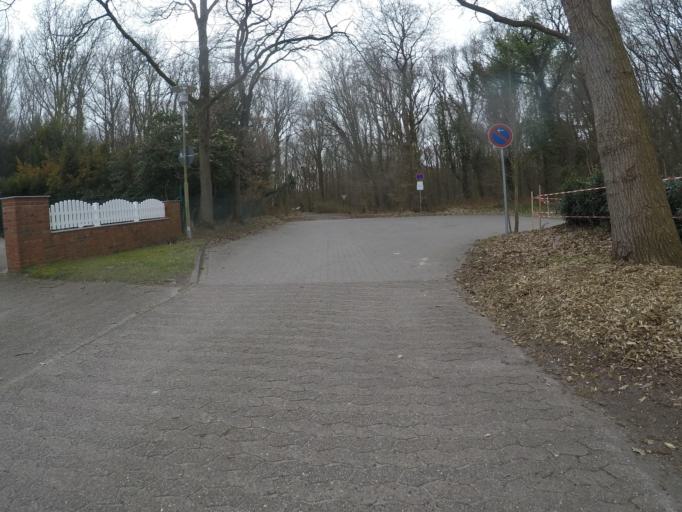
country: DE
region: Lower Saxony
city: Cuxhaven
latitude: 53.8401
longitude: 8.6365
